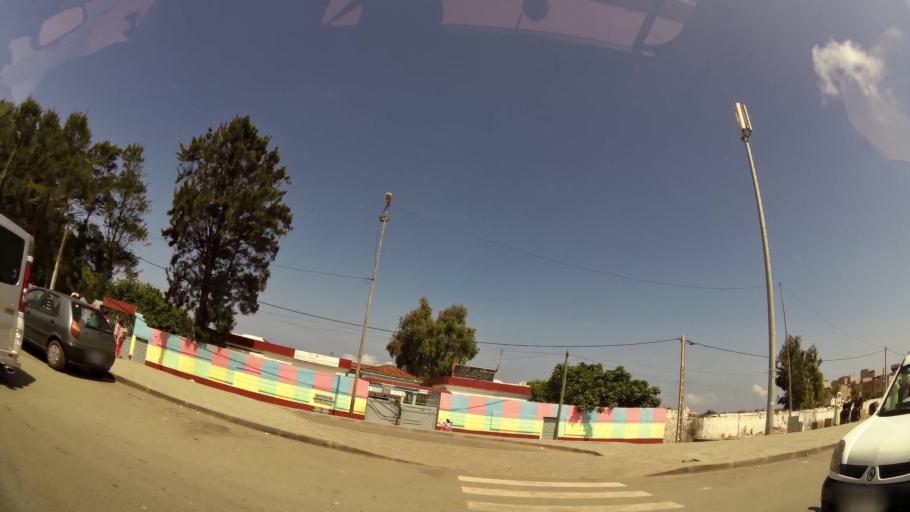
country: MA
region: Rabat-Sale-Zemmour-Zaer
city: Sale
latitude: 34.0693
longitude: -6.7774
